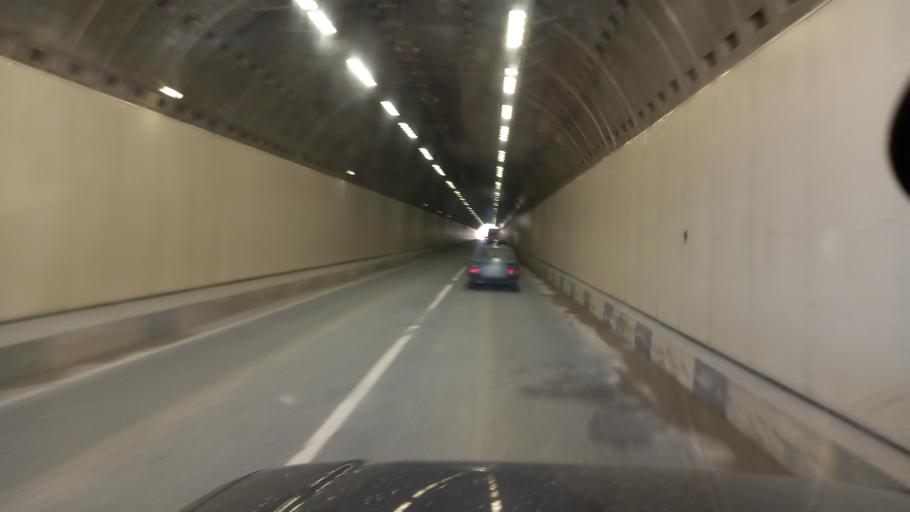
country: RU
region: Dagestan
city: Derbent
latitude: 42.0557
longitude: 48.2781
